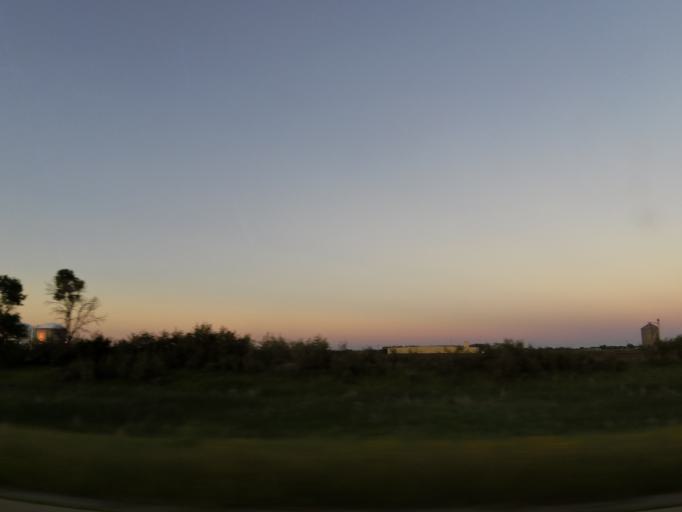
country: US
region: North Dakota
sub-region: Grand Forks County
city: Grand Forks
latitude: 47.9667
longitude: -97.0934
